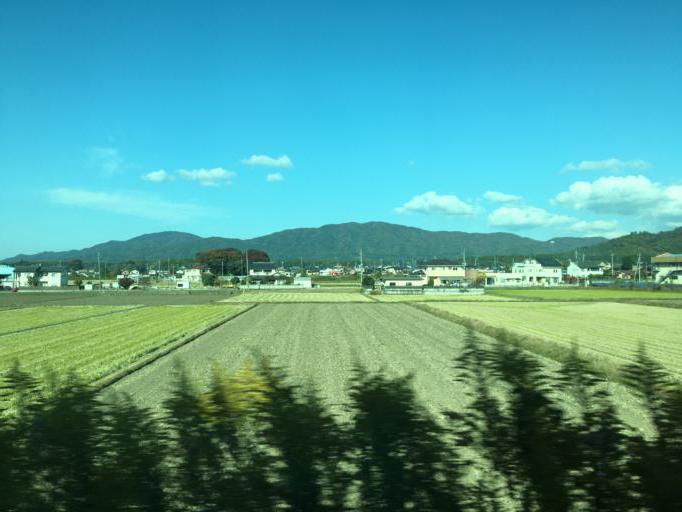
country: JP
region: Ibaraki
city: Iwase
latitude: 36.3543
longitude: 140.1504
